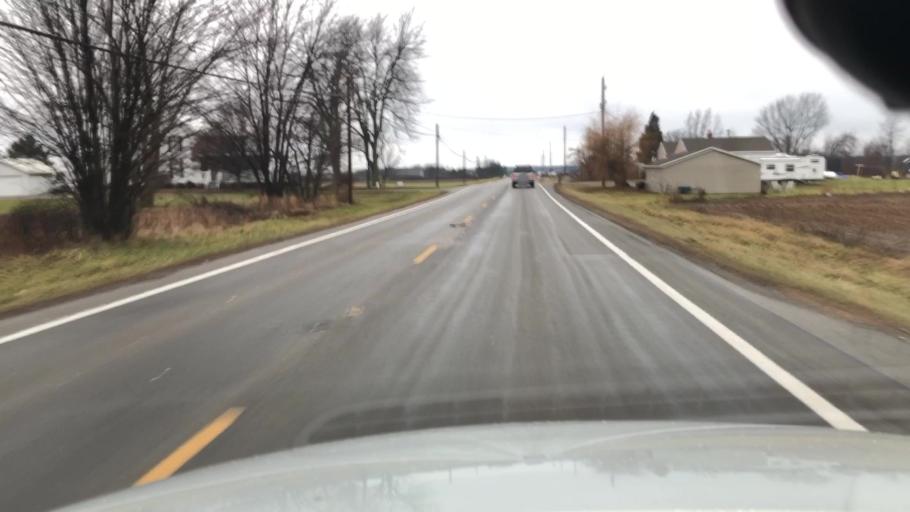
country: US
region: Ohio
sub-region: Allen County
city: Lima
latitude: 40.7058
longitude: -84.0023
